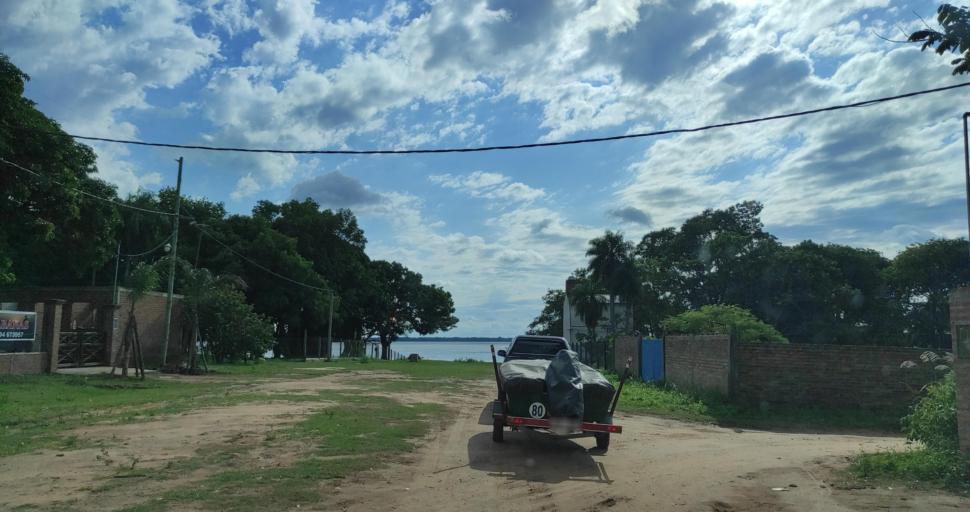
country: AR
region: Corrientes
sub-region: Departamento de Itati
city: Itati
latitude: -27.2674
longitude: -58.2521
